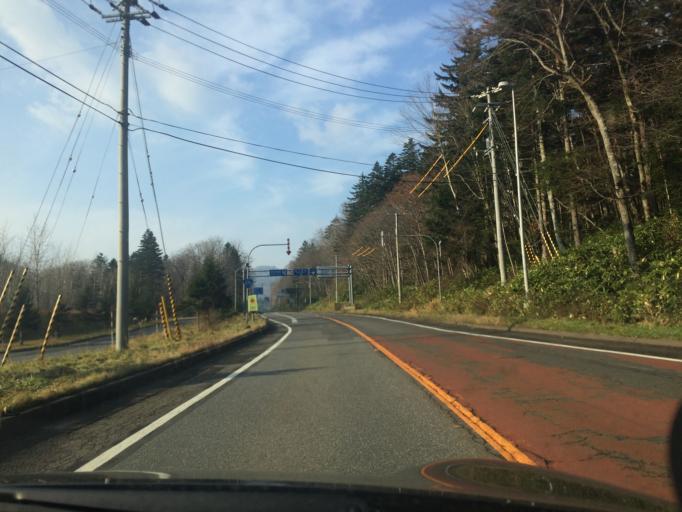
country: JP
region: Hokkaido
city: Shimo-furano
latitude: 42.9100
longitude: 142.3697
